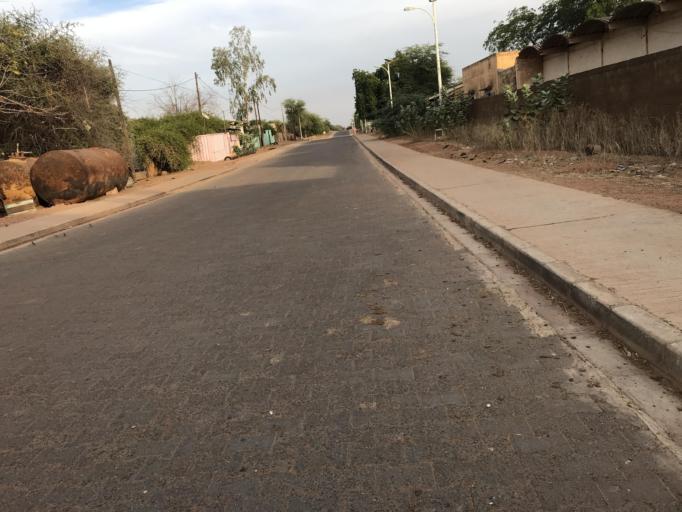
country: SN
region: Louga
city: Ndibene Dahra
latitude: 15.3998
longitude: -15.1151
